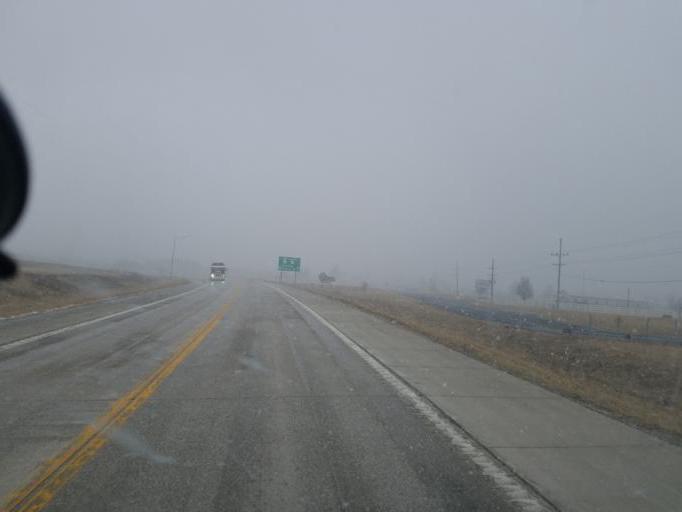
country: US
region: Missouri
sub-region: Adair County
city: Kirksville
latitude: 40.2441
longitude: -92.5824
